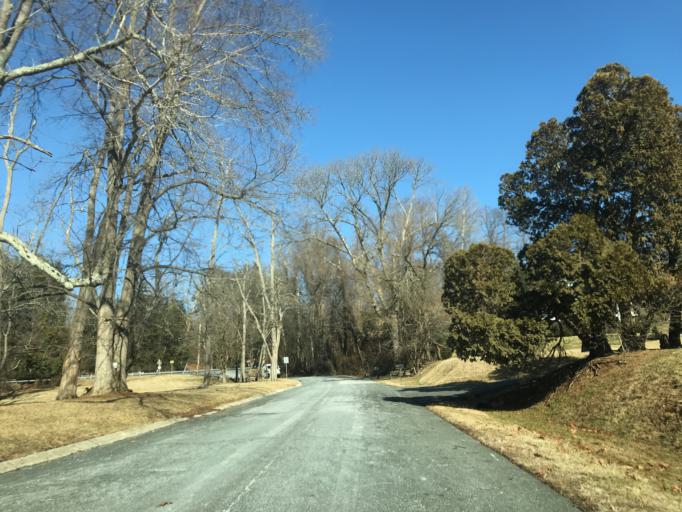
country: US
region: Maryland
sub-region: Harford County
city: North Bel Air
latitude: 39.5154
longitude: -76.3668
